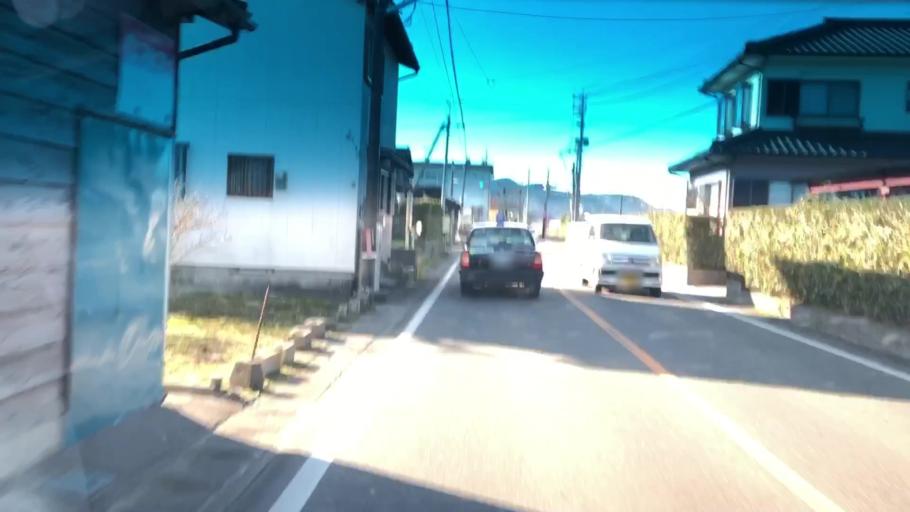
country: JP
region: Kagoshima
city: Satsumasendai
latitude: 31.8241
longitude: 130.2523
